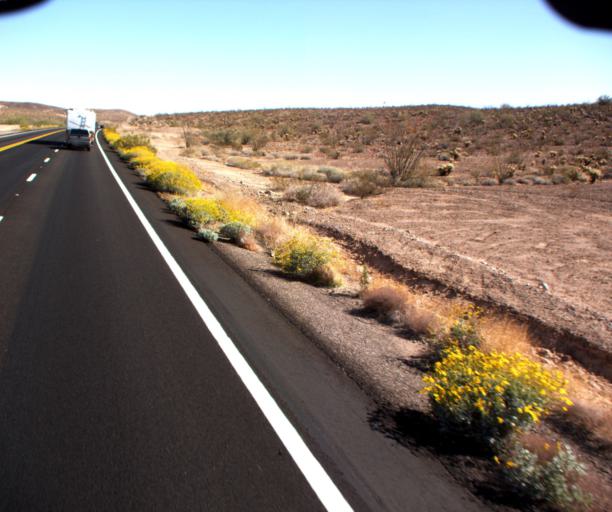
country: US
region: Arizona
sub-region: La Paz County
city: Quartzsite
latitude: 33.2269
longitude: -114.2556
